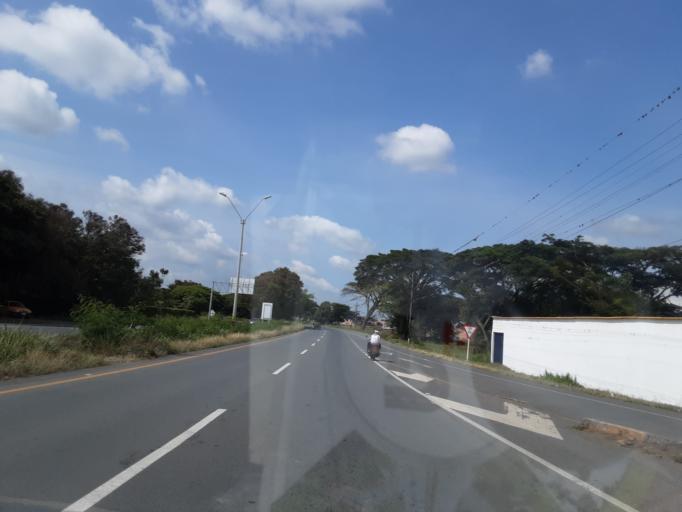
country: CO
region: Valle del Cauca
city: Guacari
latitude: 3.7597
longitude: -76.3261
